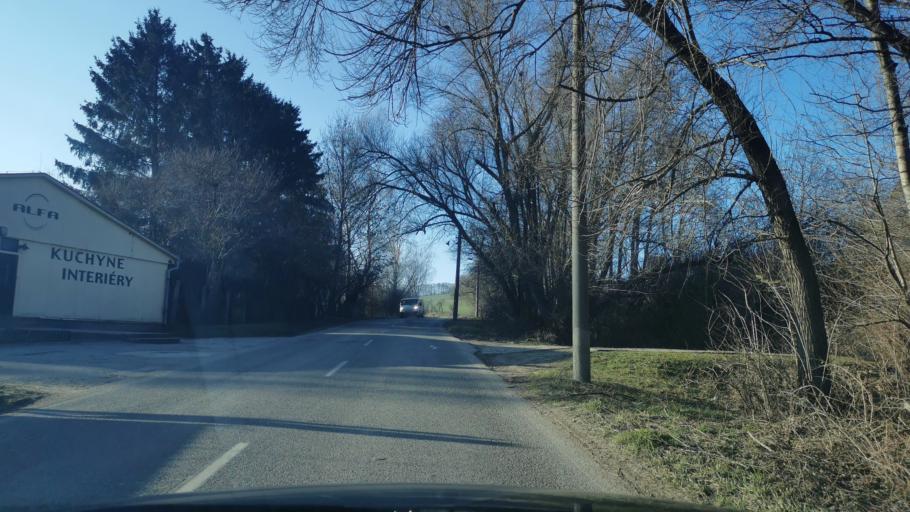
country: SK
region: Trnavsky
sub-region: Okres Senica
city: Senica
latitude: 48.7325
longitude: 17.3934
